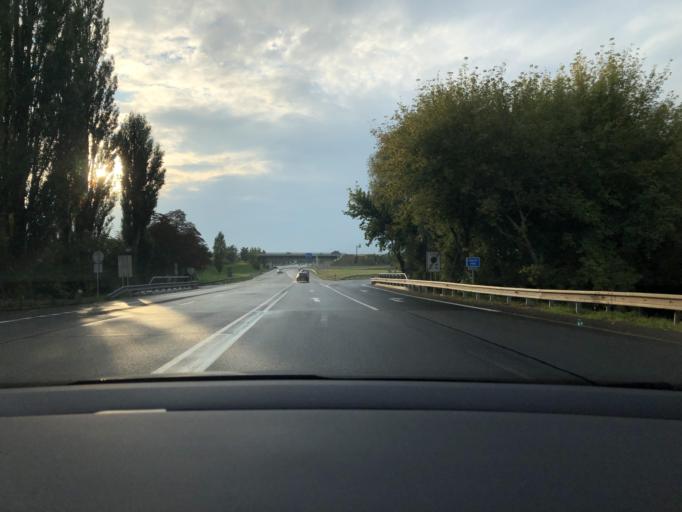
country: CZ
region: Central Bohemia
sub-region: Okres Kolin
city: Kolin
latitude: 50.0332
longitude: 15.1741
